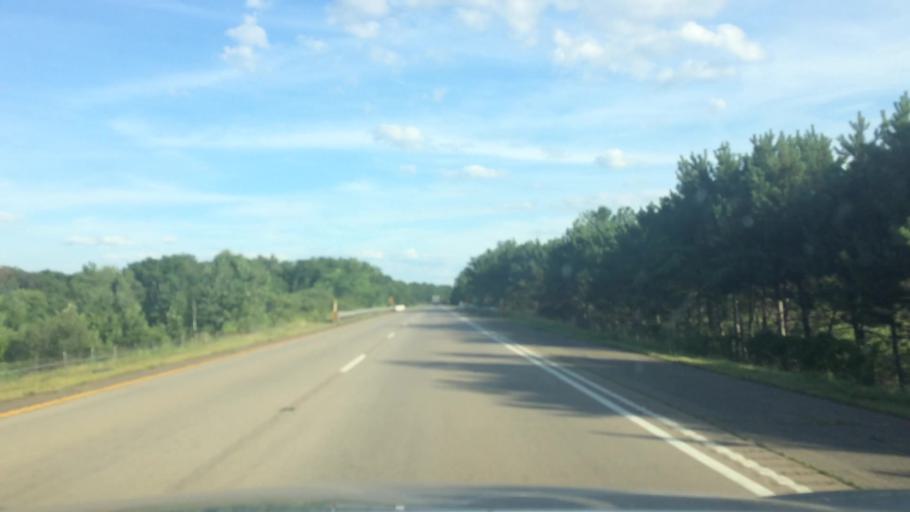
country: US
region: Wisconsin
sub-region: Marathon County
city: Mosinee
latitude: 44.6958
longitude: -89.6470
